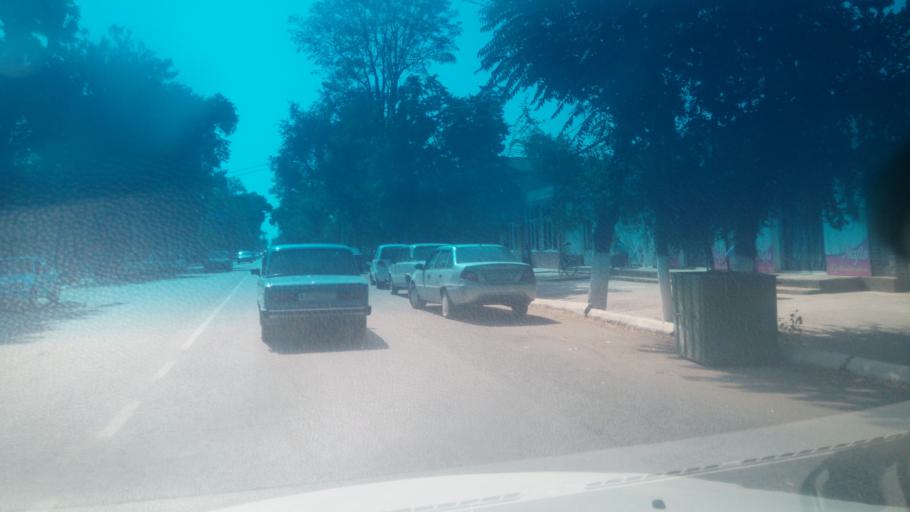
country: UZ
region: Sirdaryo
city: Sirdaryo
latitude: 40.8312
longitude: 68.6658
